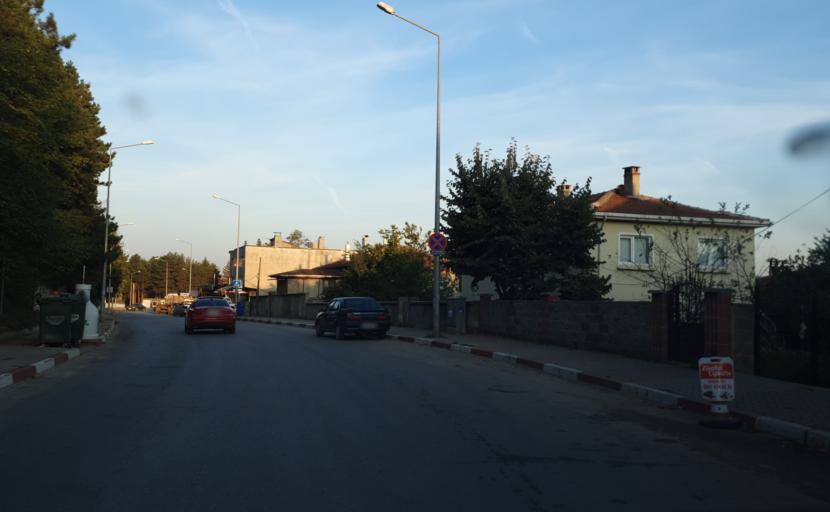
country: TR
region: Kirklareli
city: Sergen
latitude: 41.8241
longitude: 27.7711
